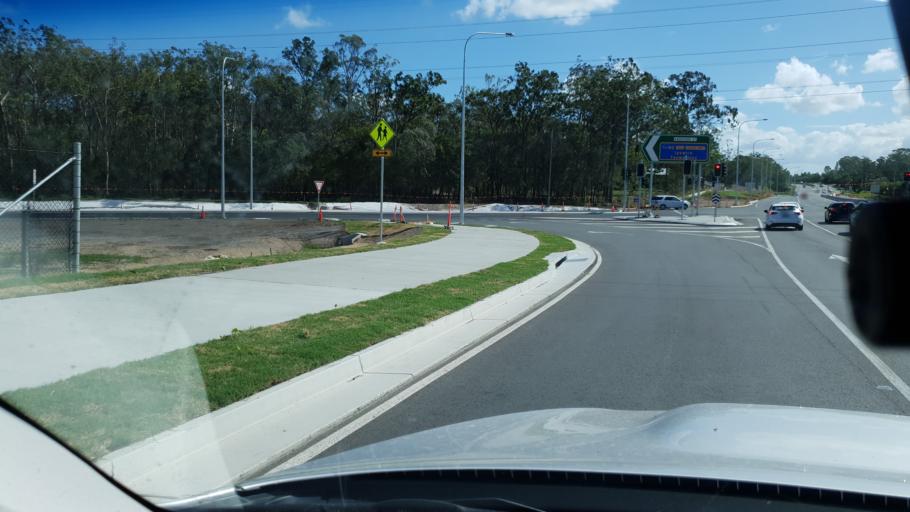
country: AU
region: Queensland
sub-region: Logan
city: Woodridge
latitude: -27.6536
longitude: 153.0691
